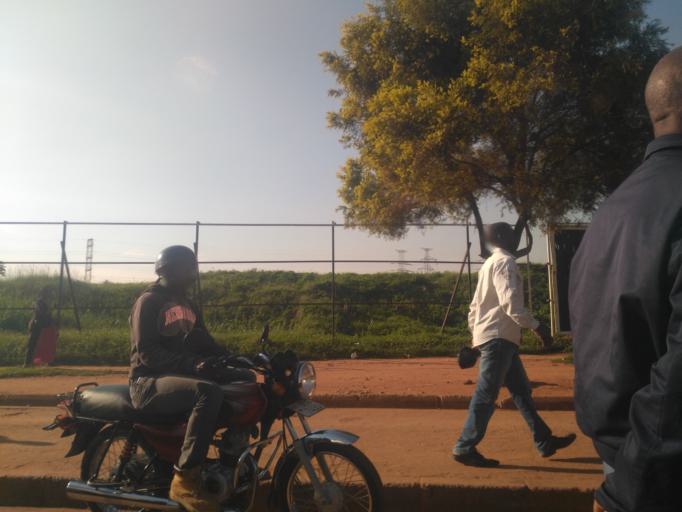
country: UG
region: Central Region
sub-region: Kampala District
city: Kampala
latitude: 0.3072
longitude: 32.5788
